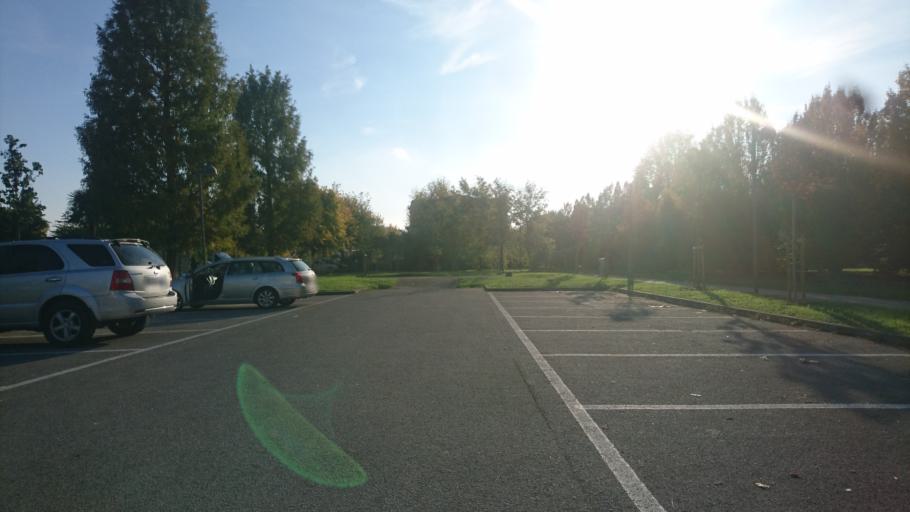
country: IT
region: Veneto
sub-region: Provincia di Padova
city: Abano Terme
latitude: 45.3479
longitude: 11.7809
